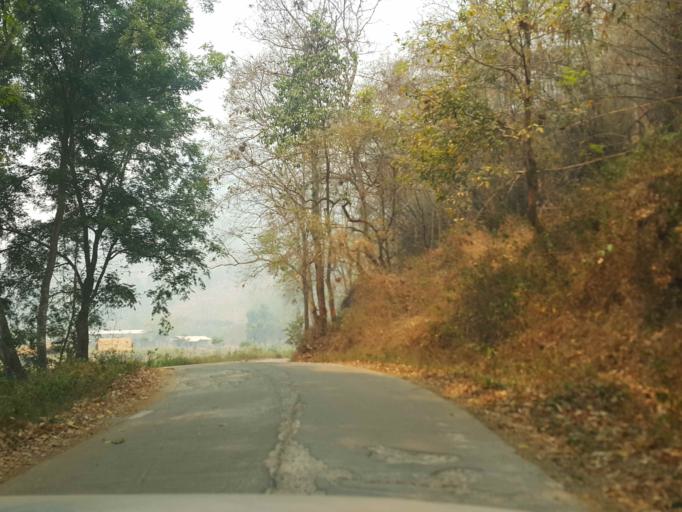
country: TH
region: Chiang Mai
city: Mae Taeng
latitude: 19.2141
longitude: 98.8713
